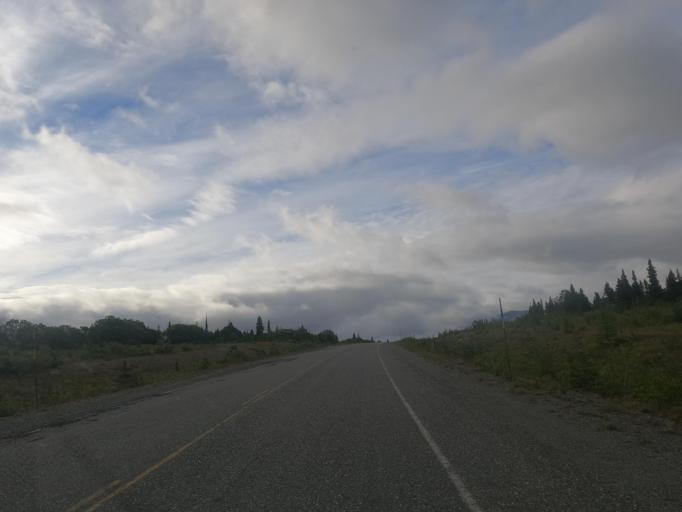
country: CA
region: Yukon
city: Haines Junction
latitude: 59.9448
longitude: -136.8010
